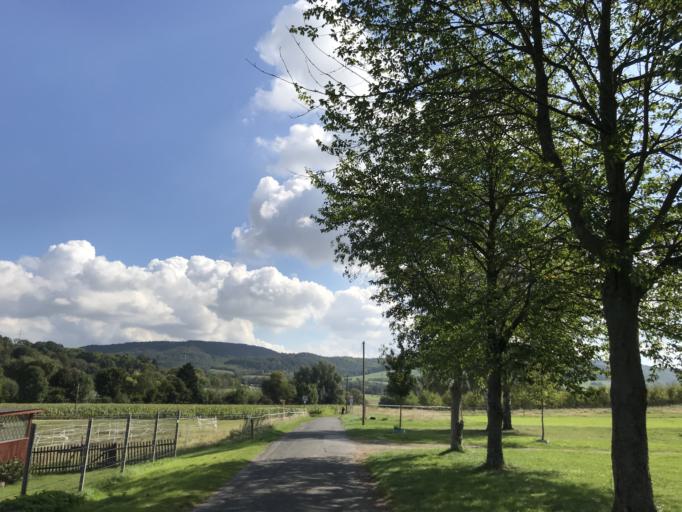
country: DE
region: Hesse
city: Witzenhausen
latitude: 51.3471
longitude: 9.8698
